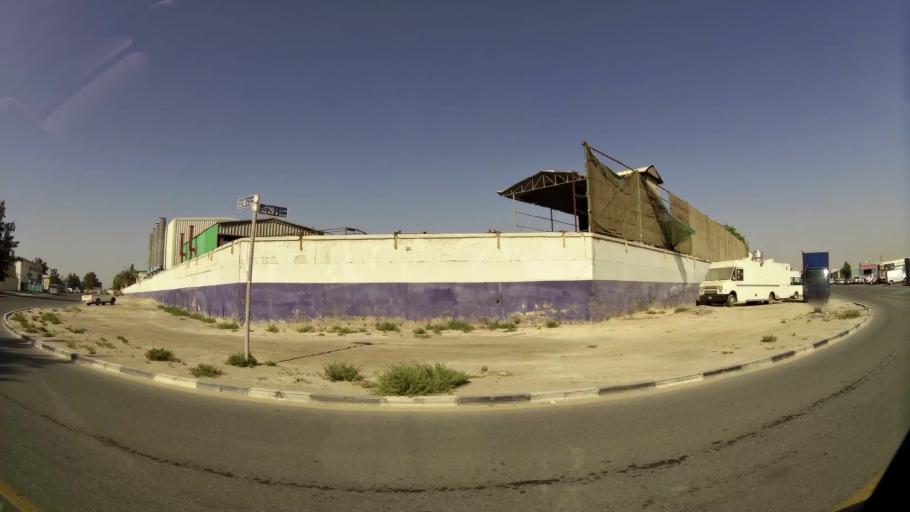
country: AE
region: Dubai
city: Dubai
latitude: 25.1203
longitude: 55.2083
